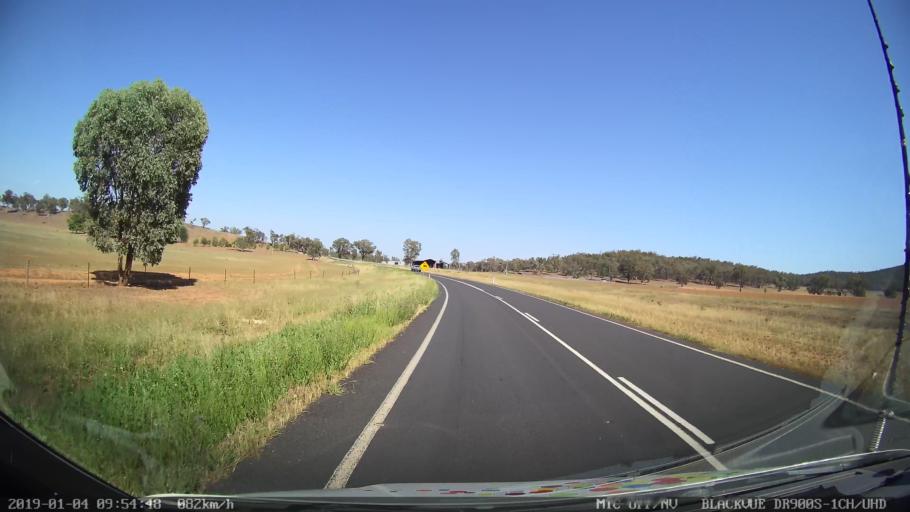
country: AU
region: New South Wales
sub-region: Cabonne
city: Canowindra
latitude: -33.5382
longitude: 148.4108
